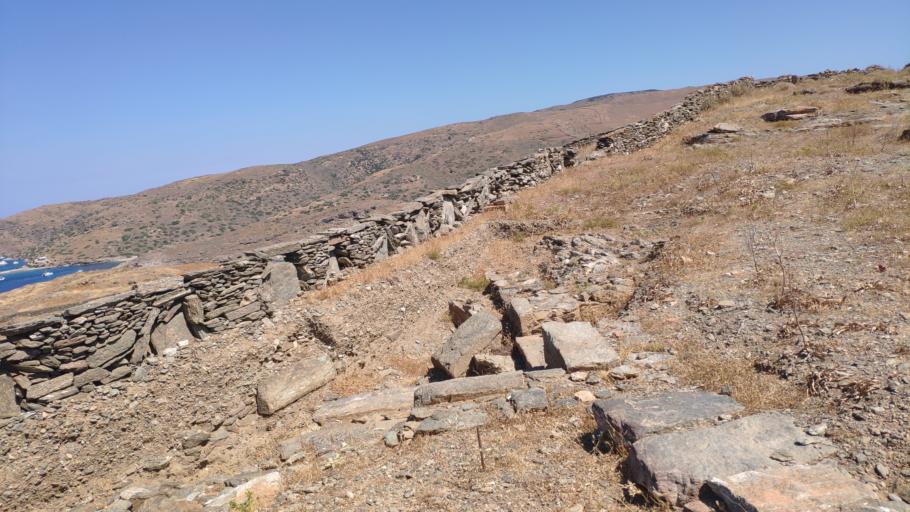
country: GR
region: South Aegean
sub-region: Nomos Kykladon
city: Kythnos
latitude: 37.4075
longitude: 24.3950
